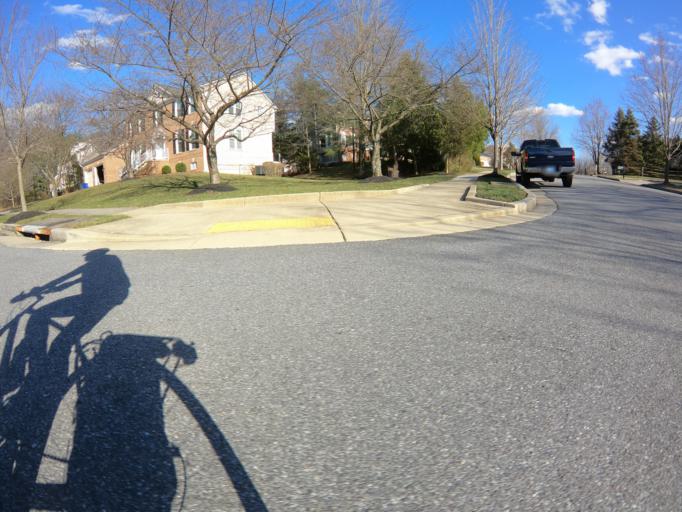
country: US
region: Maryland
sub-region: Howard County
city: Ellicott City
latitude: 39.2544
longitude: -76.8027
